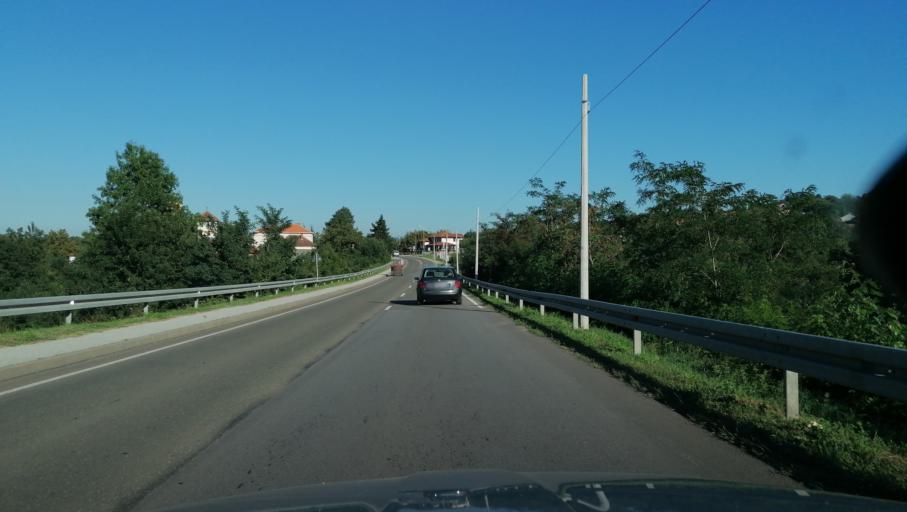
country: RS
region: Central Serbia
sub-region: Sumadijski Okrug
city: Knic
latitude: 43.9279
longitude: 20.7094
